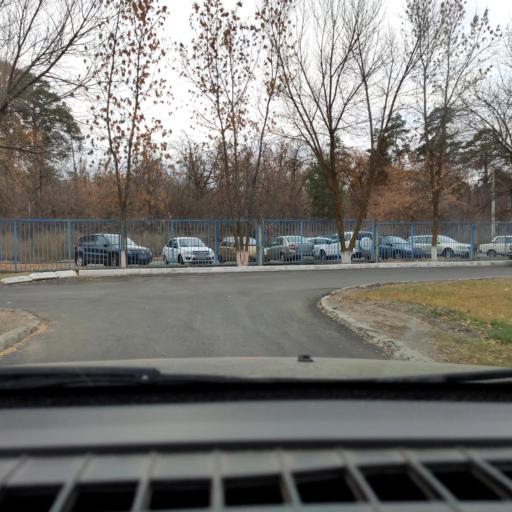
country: RU
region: Samara
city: Tol'yatti
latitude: 53.5206
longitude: 49.3269
